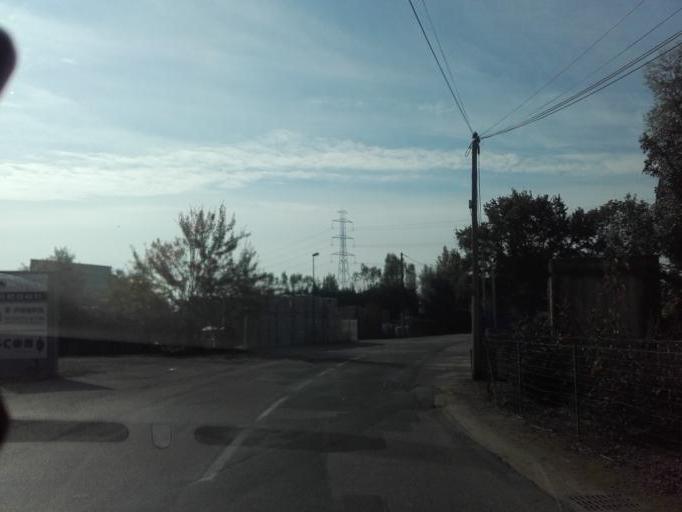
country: FR
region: Bourgogne
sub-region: Departement de Saone-et-Loire
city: La Chapelle-de-Guinchay
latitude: 46.2199
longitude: 4.7440
